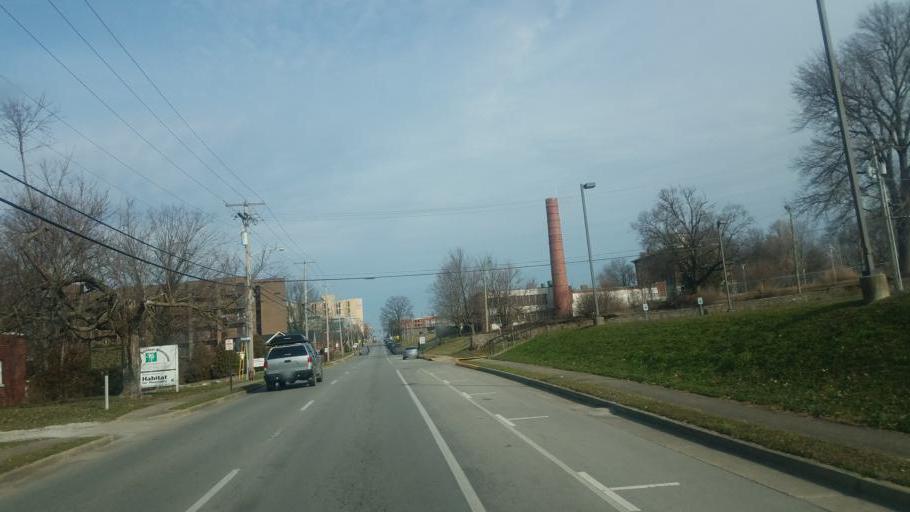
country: US
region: Kentucky
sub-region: Boyle County
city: Danville
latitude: 37.6401
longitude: -84.7731
